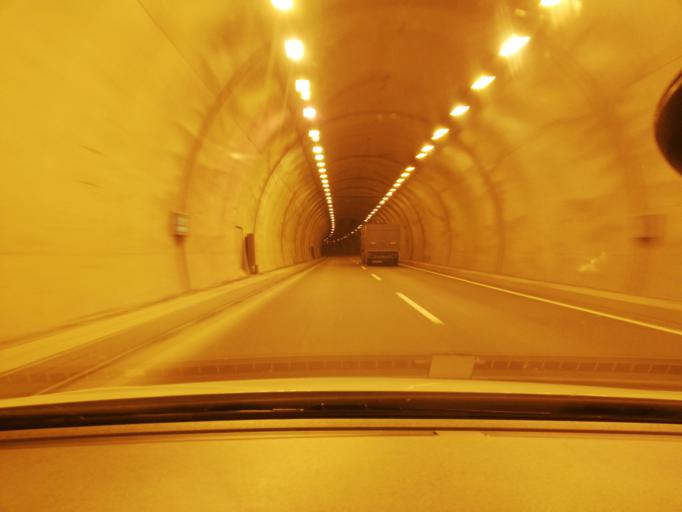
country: TR
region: Zonguldak
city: Alapli
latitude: 41.1542
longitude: 31.3545
